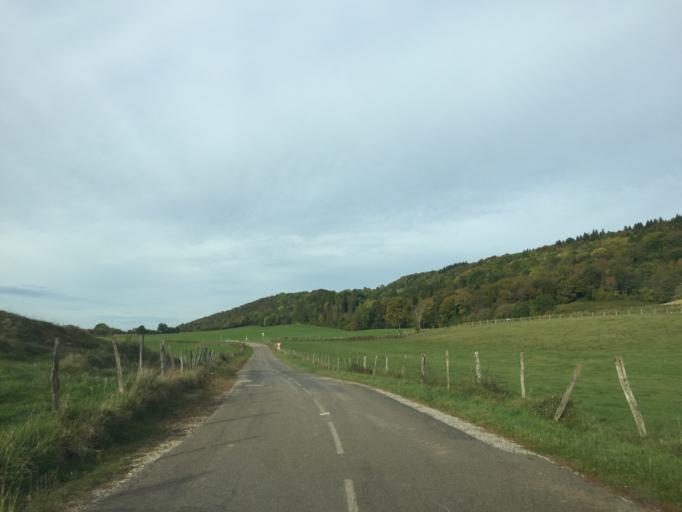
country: FR
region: Franche-Comte
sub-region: Departement du Jura
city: Orgelet
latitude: 46.5455
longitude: 5.5304
